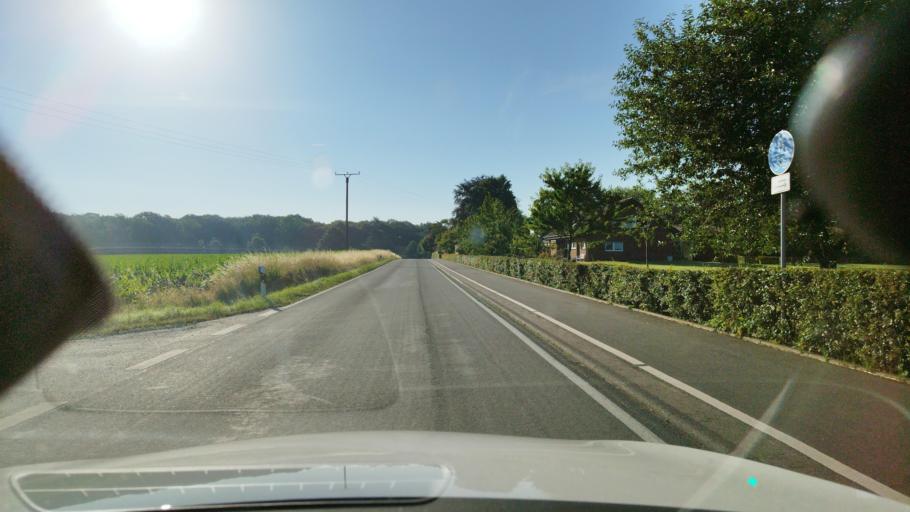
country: DE
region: North Rhine-Westphalia
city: Datteln
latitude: 51.6707
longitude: 7.4251
